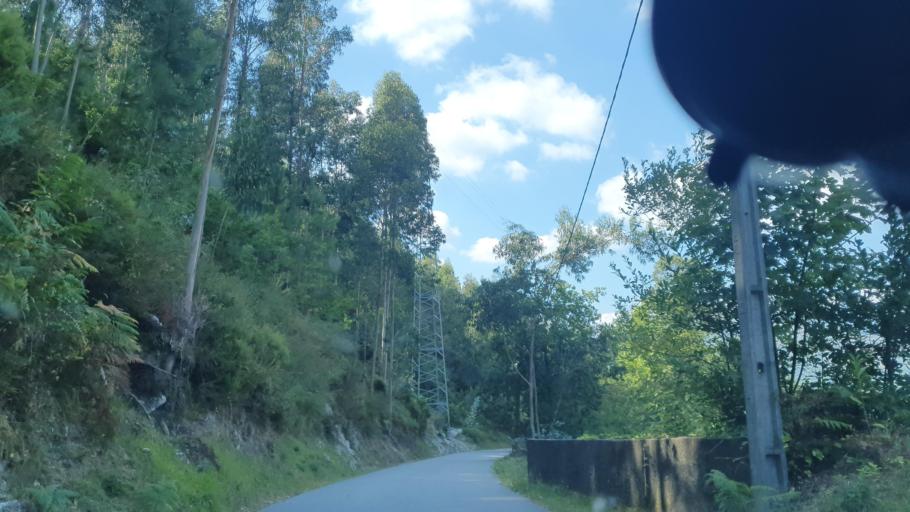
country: PT
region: Braga
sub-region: Vieira do Minho
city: Real
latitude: 41.6687
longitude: -8.1693
